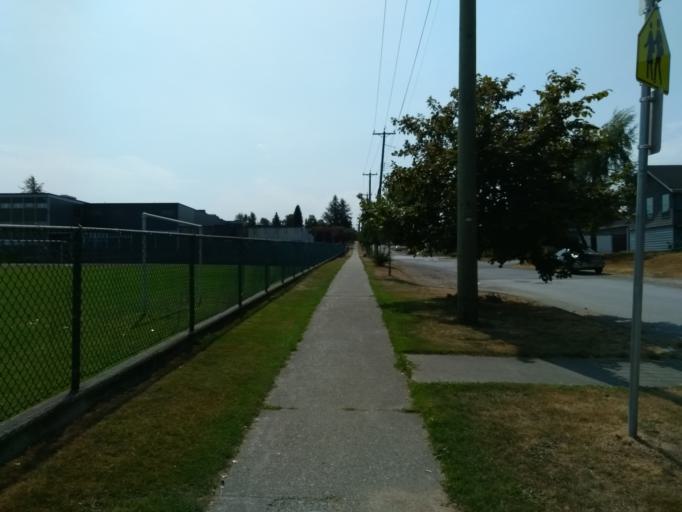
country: CA
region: British Columbia
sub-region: Fraser Valley Regional District
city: North Vancouver
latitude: 49.2479
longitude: -123.0390
